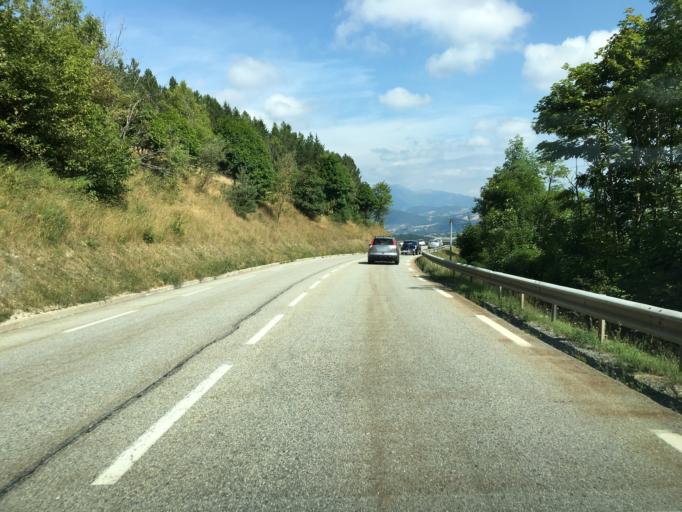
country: FR
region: Rhone-Alpes
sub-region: Departement de l'Isere
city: Mens
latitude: 44.7428
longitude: 5.6812
